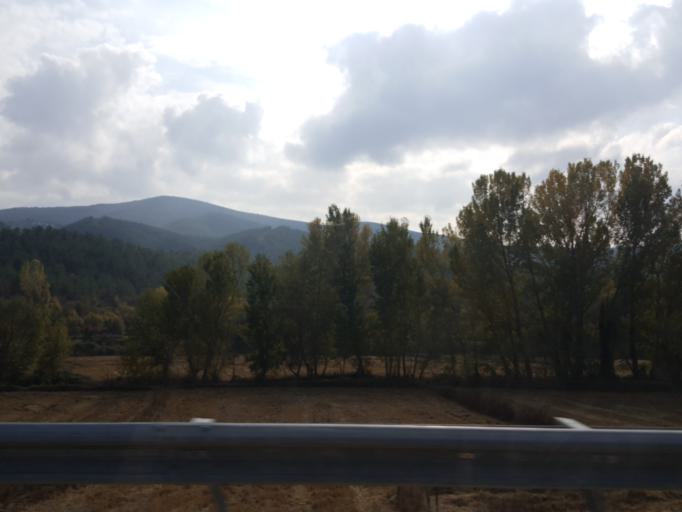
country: TR
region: Sinop
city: Sarayduzu
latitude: 41.3850
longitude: 34.9276
